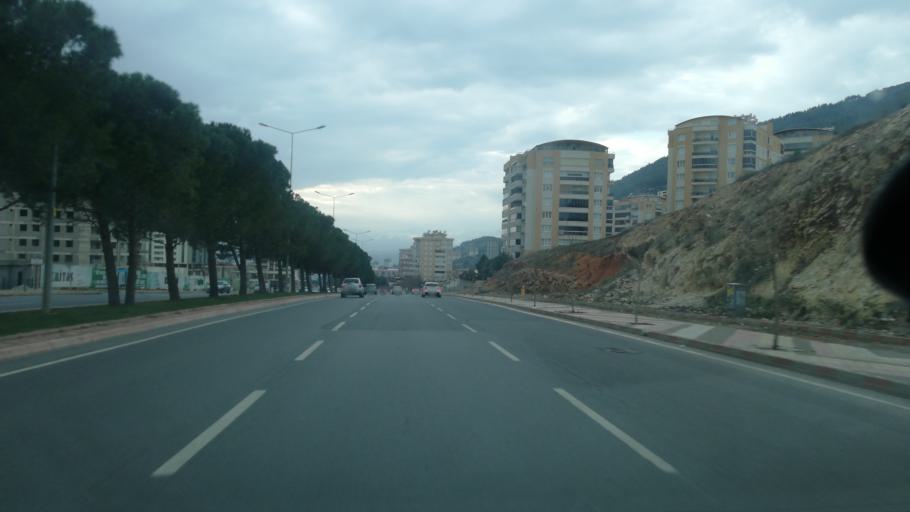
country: TR
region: Kahramanmaras
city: Kahramanmaras
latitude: 37.5963
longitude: 36.8500
